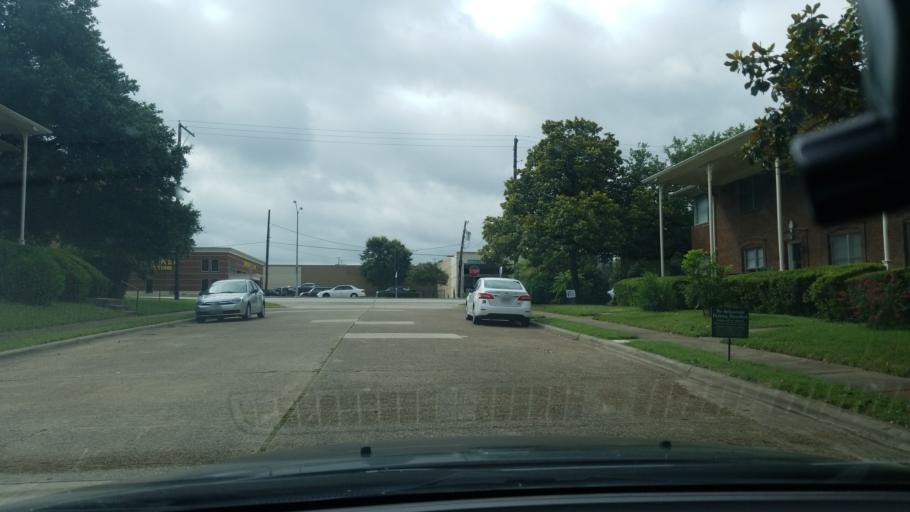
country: US
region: Texas
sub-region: Dallas County
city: Highland Park
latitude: 32.8260
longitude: -96.7126
